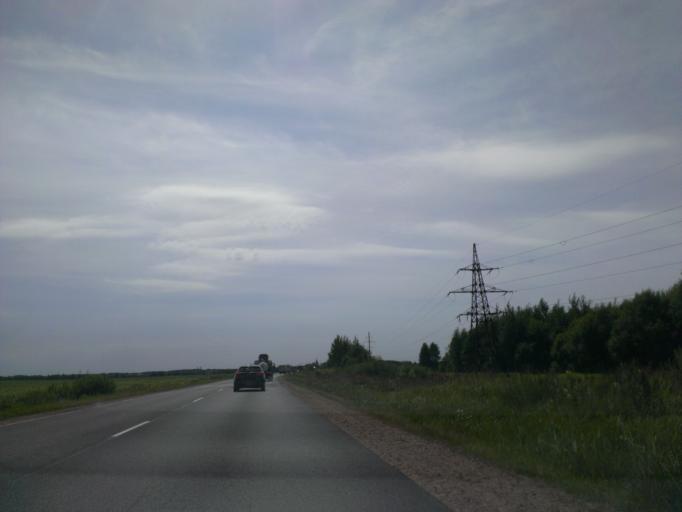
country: LV
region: Salaspils
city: Salaspils
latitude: 56.8650
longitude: 24.4063
